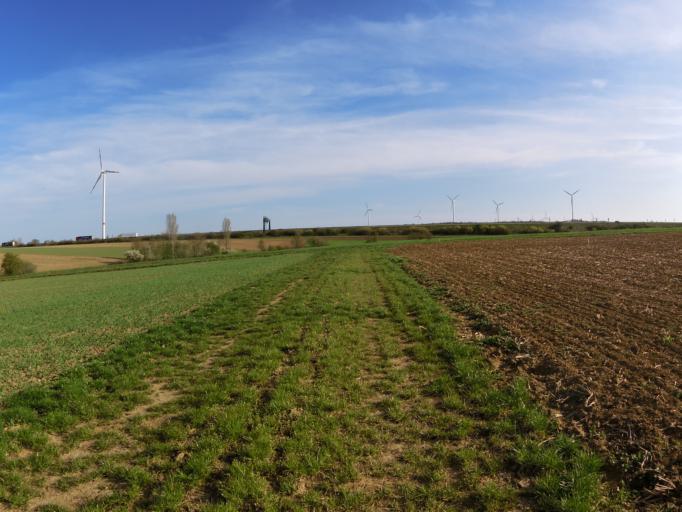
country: DE
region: Bavaria
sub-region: Regierungsbezirk Unterfranken
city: Biebelried
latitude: 49.7868
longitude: 10.1097
